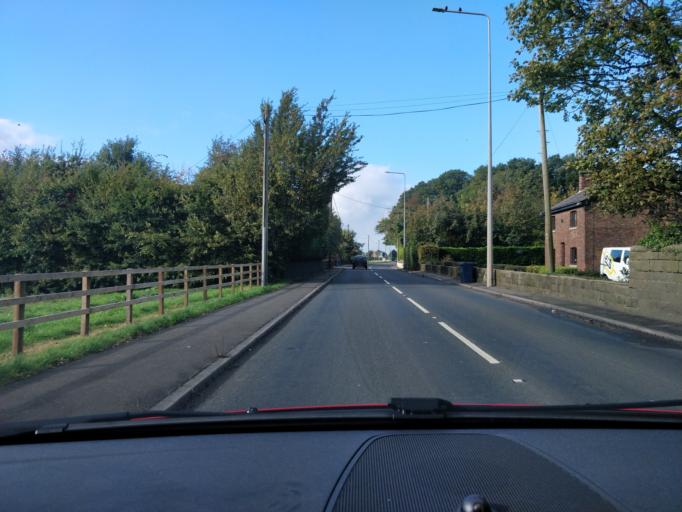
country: GB
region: England
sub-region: Lancashire
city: Ormskirk
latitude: 53.6025
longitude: -2.9298
